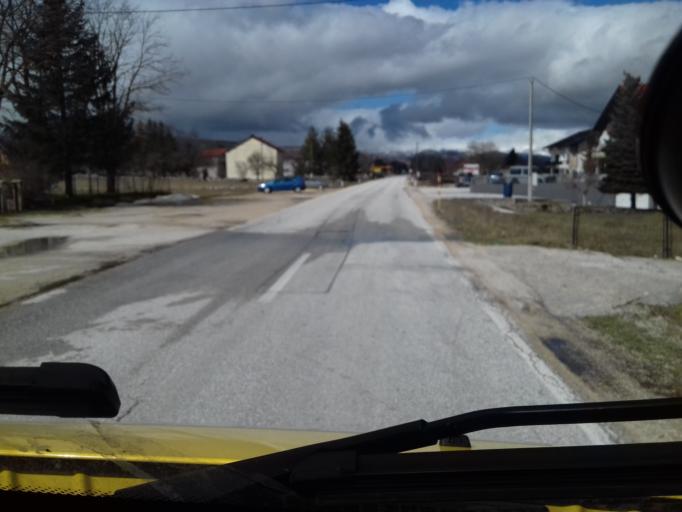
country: BA
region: Federation of Bosnia and Herzegovina
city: Dreznica
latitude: 43.6219
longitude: 17.2584
